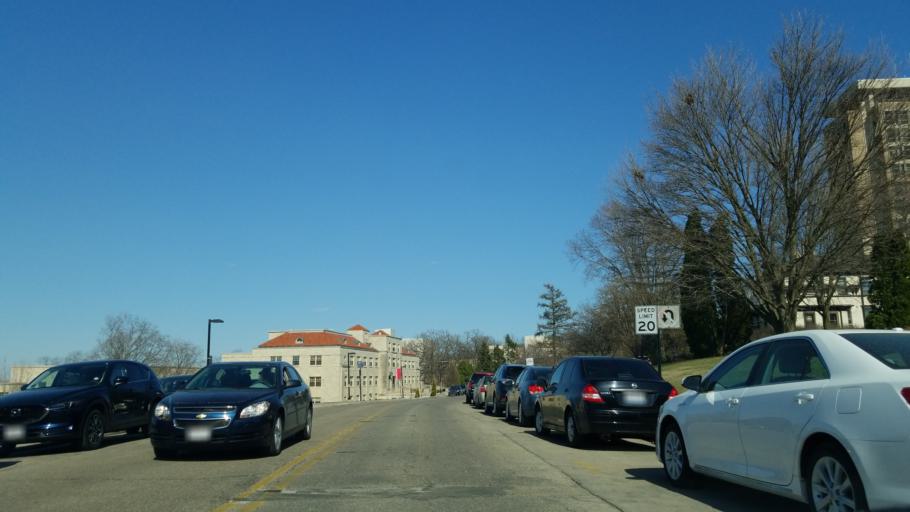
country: US
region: Wisconsin
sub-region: Dane County
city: Madison
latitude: 43.0765
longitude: -89.4086
